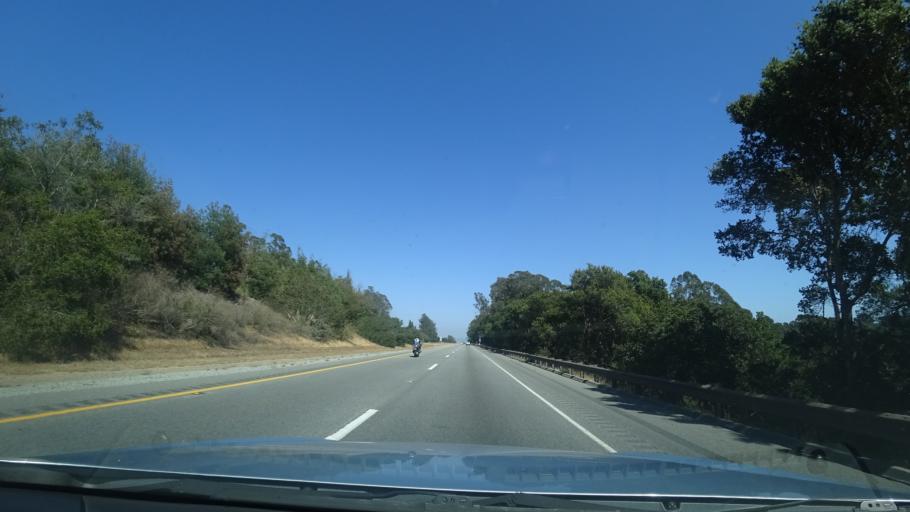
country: US
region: California
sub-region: Santa Cruz County
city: Aptos Hills-Larkin Valley
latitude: 36.9369
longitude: -121.8293
